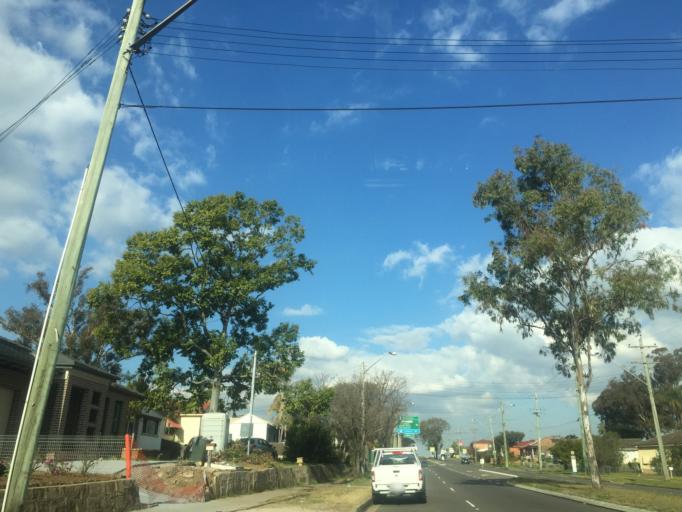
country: AU
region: New South Wales
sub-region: Blacktown
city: Quakers Hill
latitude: -33.7552
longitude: 150.8916
